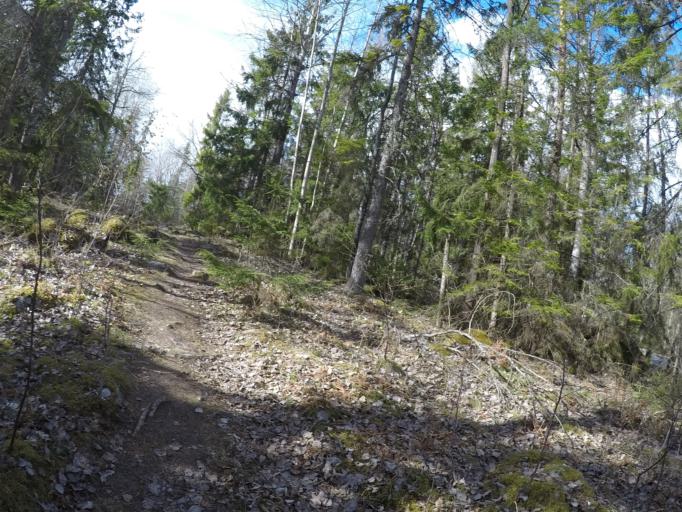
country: SE
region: Soedermanland
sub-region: Eskilstuna Kommun
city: Kvicksund
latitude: 59.4649
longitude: 16.3207
